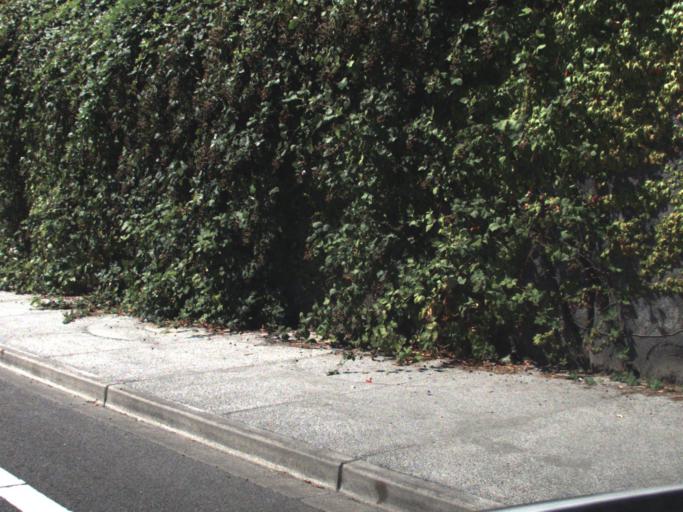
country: US
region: Washington
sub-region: King County
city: Issaquah
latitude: 47.5374
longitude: -122.0629
